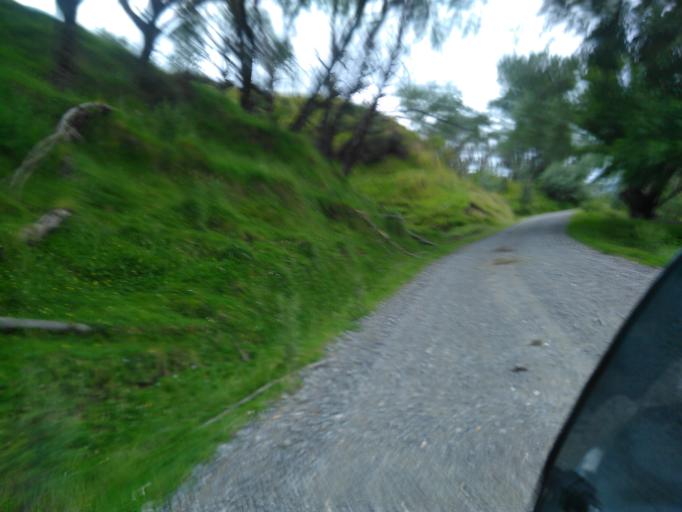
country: NZ
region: Gisborne
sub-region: Gisborne District
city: Gisborne
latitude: -38.0750
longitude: 178.0512
